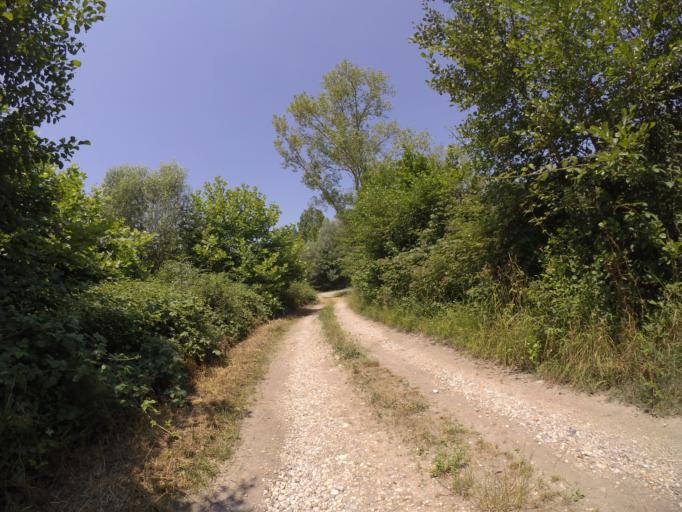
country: IT
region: Friuli Venezia Giulia
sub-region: Provincia di Udine
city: Rivignano
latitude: 45.9023
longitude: 13.0358
